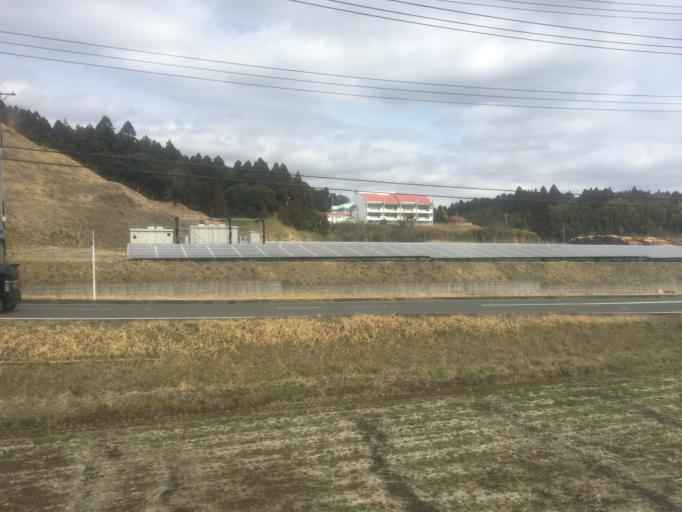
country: JP
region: Chiba
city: Yachimata
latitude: 35.6459
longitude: 140.3438
